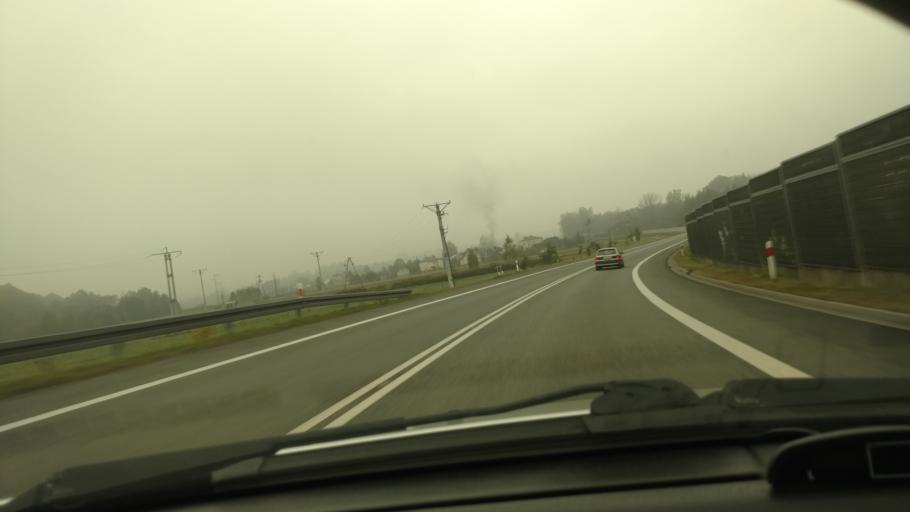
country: PL
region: Lesser Poland Voivodeship
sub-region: Powiat gorlicki
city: Biecz
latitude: 49.7115
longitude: 21.2459
